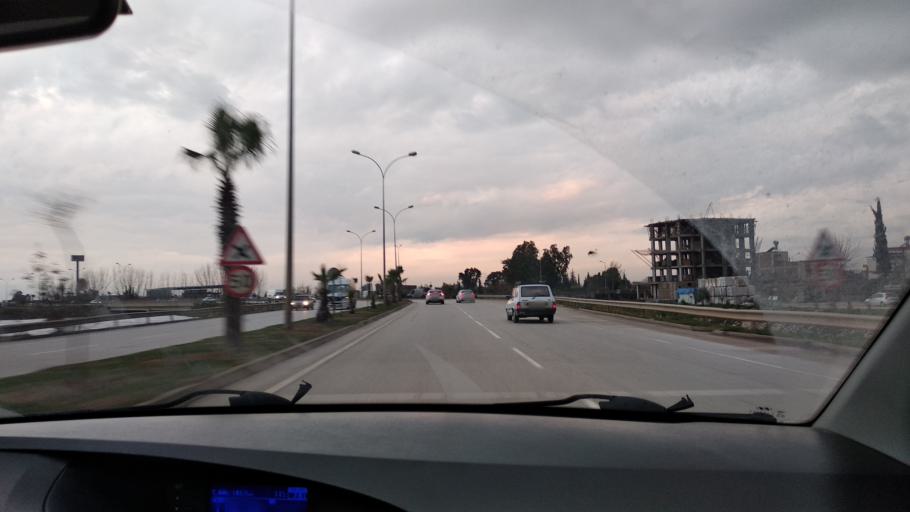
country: TR
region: Adana
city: Yuregir
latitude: 37.0100
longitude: 35.3925
